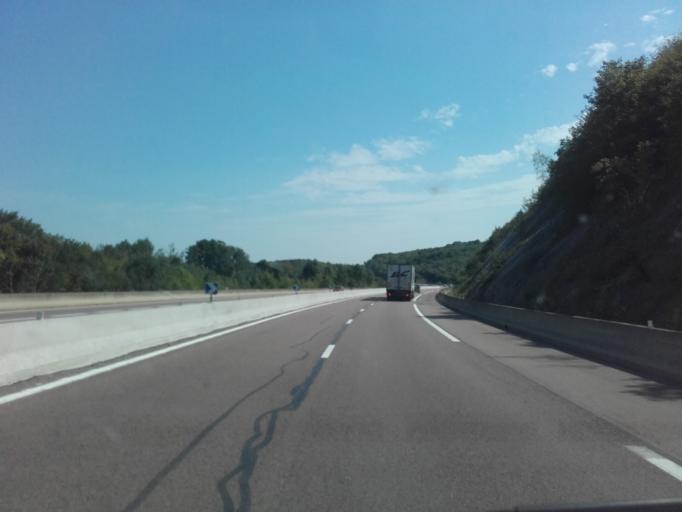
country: FR
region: Bourgogne
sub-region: Departement de la Cote-d'Or
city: Savigny-les-Beaune
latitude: 47.0825
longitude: 4.7628
